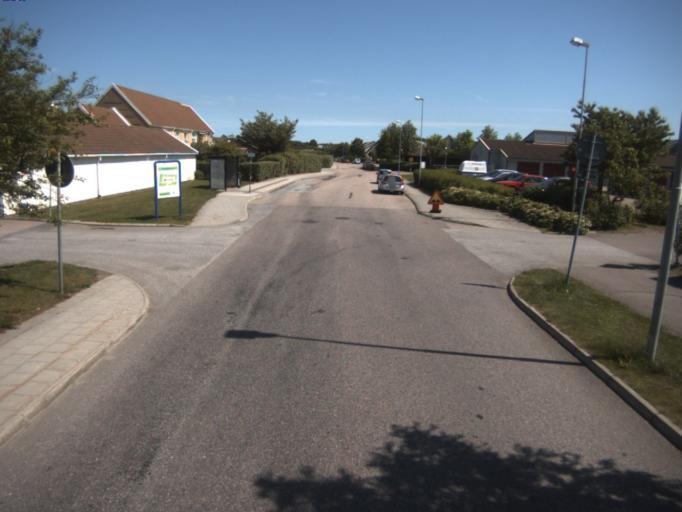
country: SE
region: Skane
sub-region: Helsingborg
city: Rydeback
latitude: 56.0050
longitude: 12.7573
